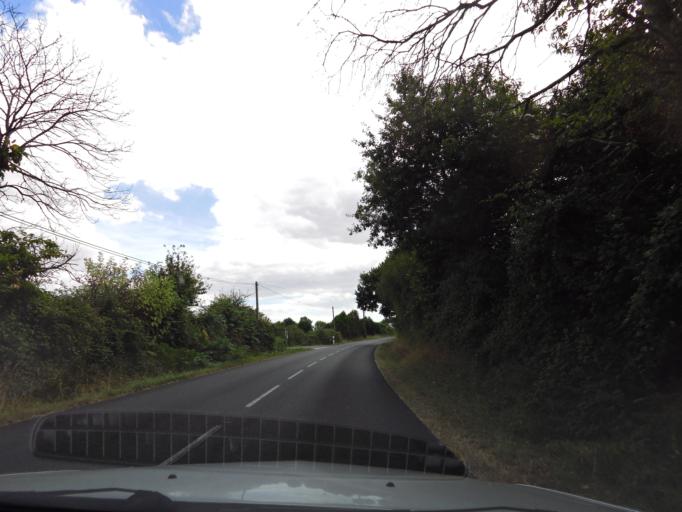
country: FR
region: Pays de la Loire
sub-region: Departement de la Vendee
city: Moutiers-les-Mauxfaits
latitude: 46.4832
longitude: -1.4419
